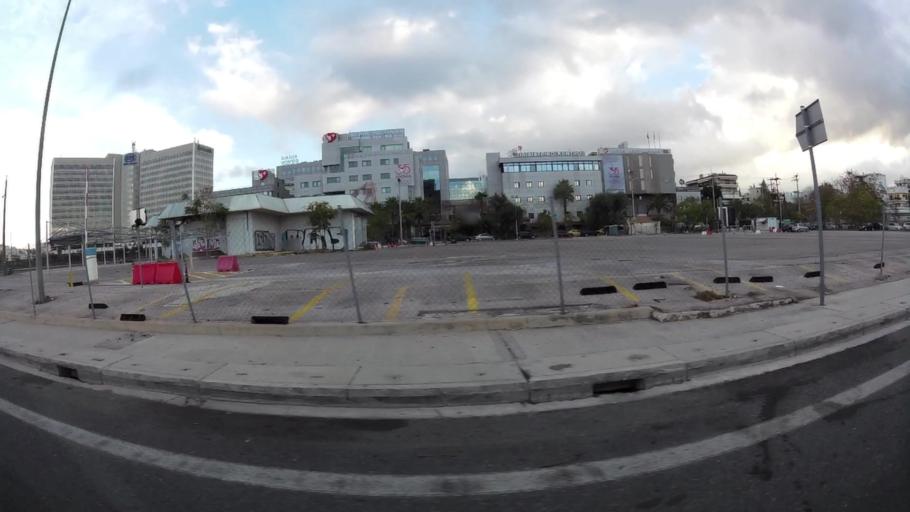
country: GR
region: Attica
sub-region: Nomarchia Athinas
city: Marousi
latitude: 38.0422
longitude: 23.8047
